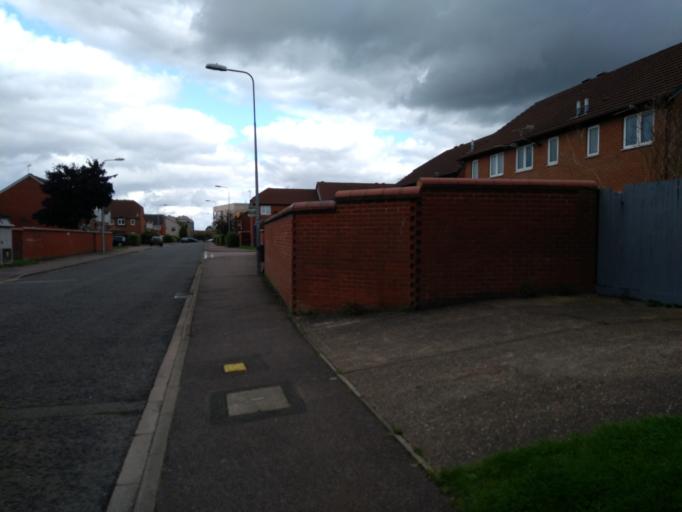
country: GB
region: England
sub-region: Central Bedfordshire
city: Houghton Regis
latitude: 51.9034
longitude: -0.5037
